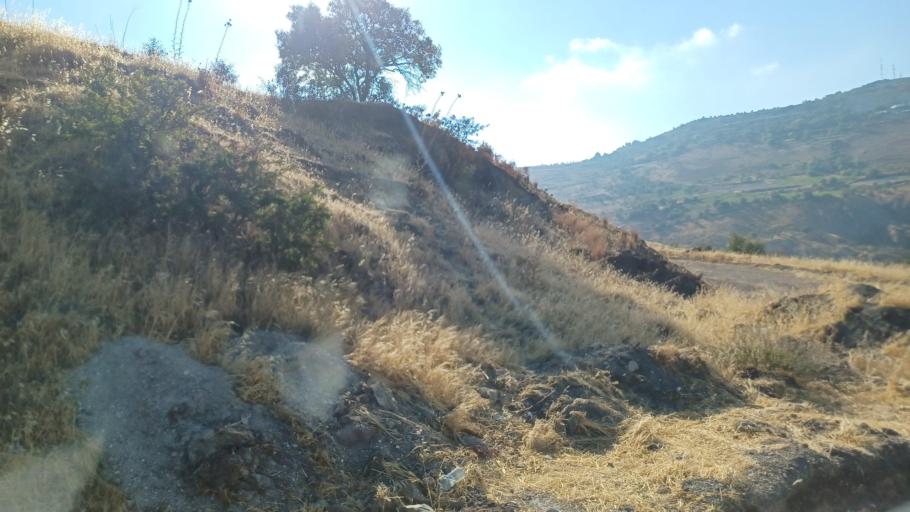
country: CY
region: Pafos
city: Mesogi
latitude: 34.8713
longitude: 32.6093
